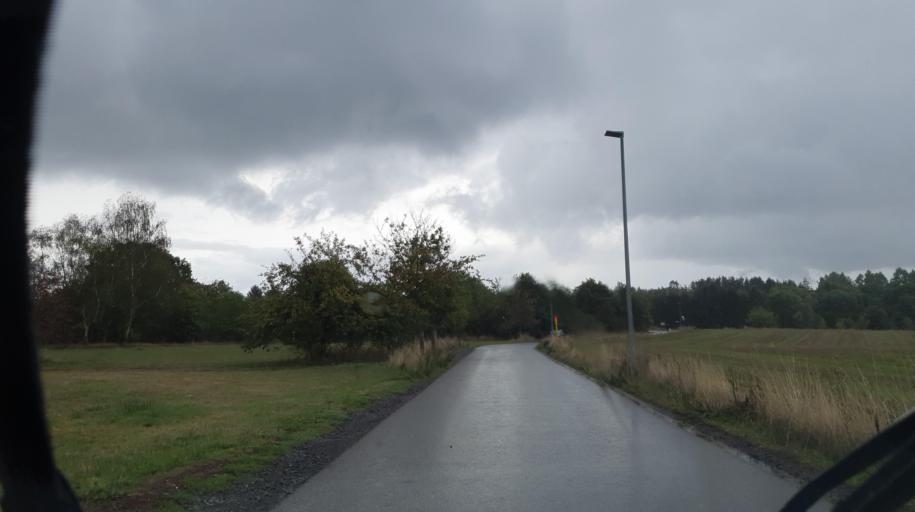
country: DE
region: Saarland
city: Spiesen-Elversberg
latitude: 49.3111
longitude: 7.1663
